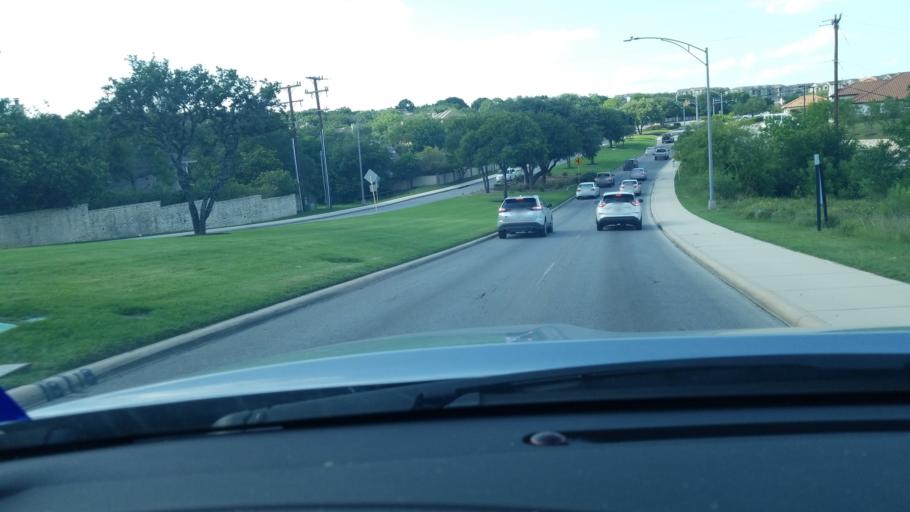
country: US
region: Texas
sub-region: Bexar County
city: Hollywood Park
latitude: 29.6369
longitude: -98.4955
